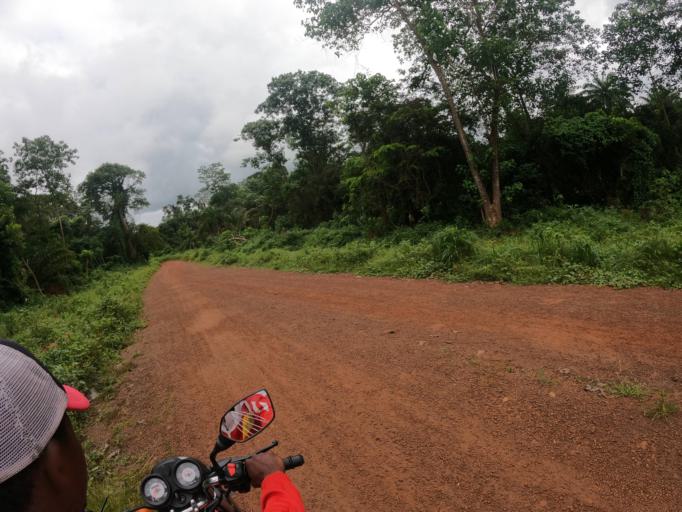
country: SL
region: Northern Province
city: Kamakwie
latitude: 9.5061
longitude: -12.2614
